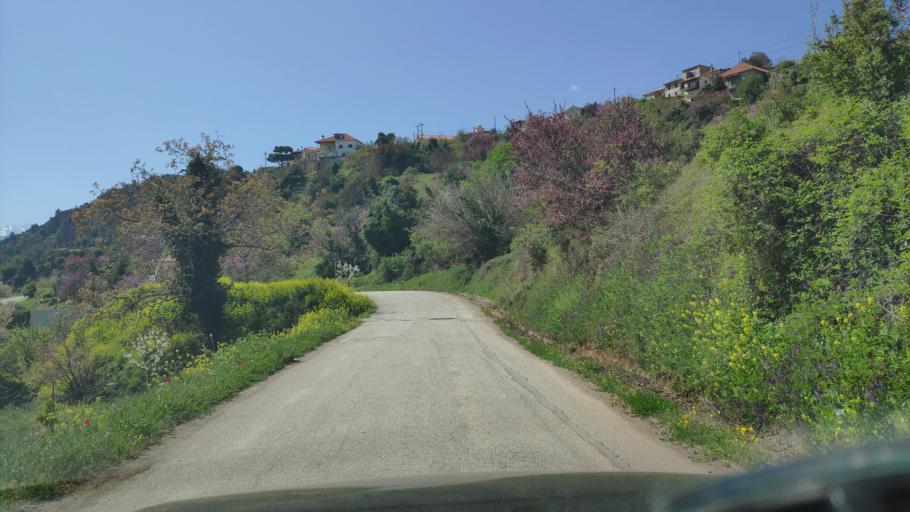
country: GR
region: West Greece
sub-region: Nomos Achaias
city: Akrata
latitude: 38.1012
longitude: 22.3180
